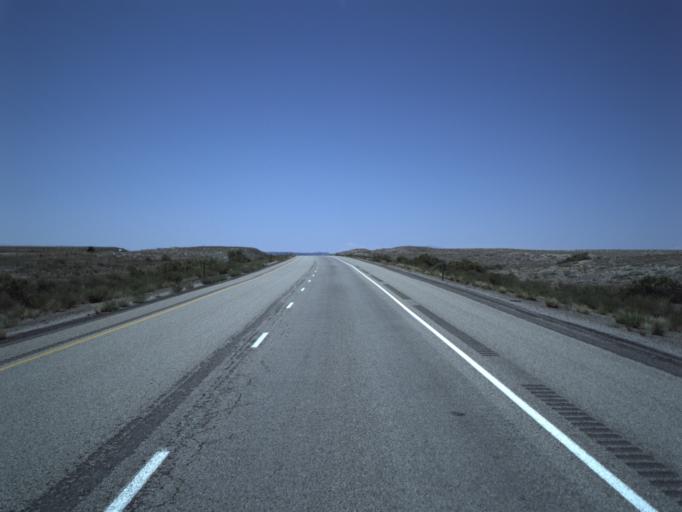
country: US
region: Utah
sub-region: Grand County
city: Moab
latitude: 38.9962
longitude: -109.3274
